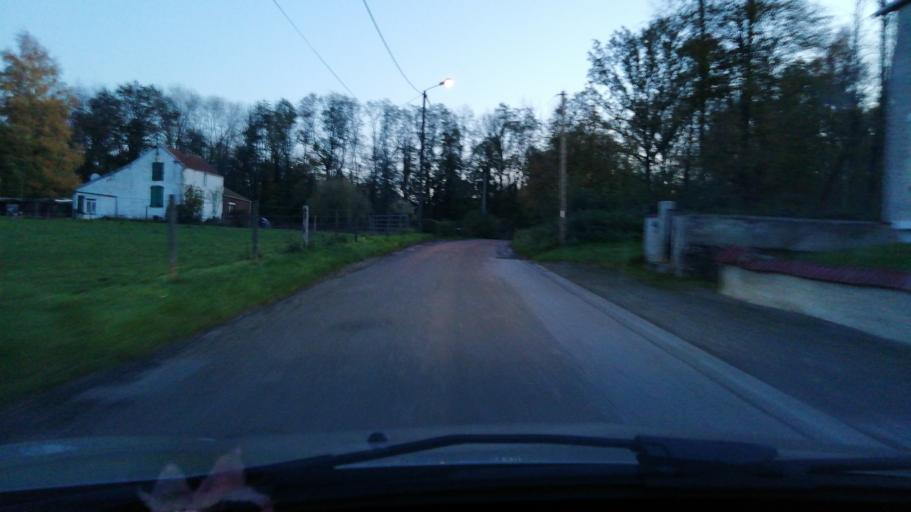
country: FR
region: Nord-Pas-de-Calais
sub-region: Departement du Nord
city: Marpent
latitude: 50.2780
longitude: 4.0889
